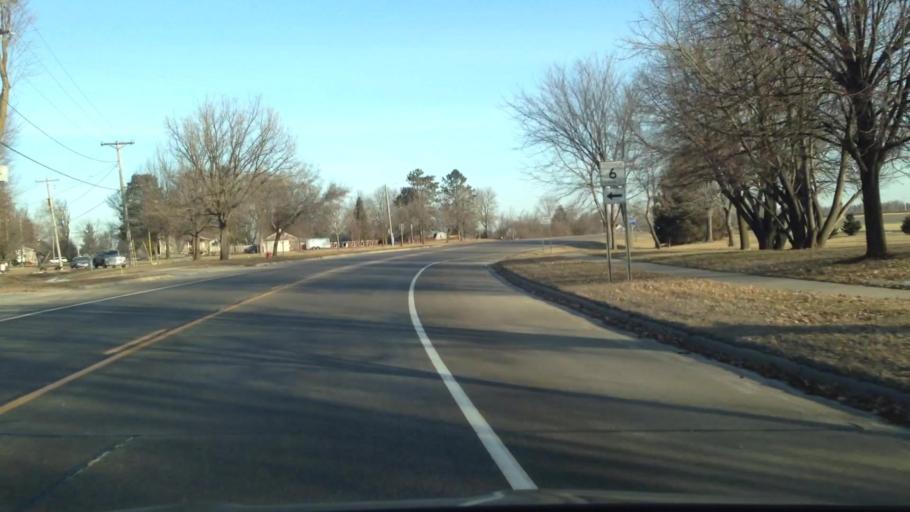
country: US
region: Minnesota
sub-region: Goodhue County
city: Zumbrota
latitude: 44.2997
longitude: -92.6692
